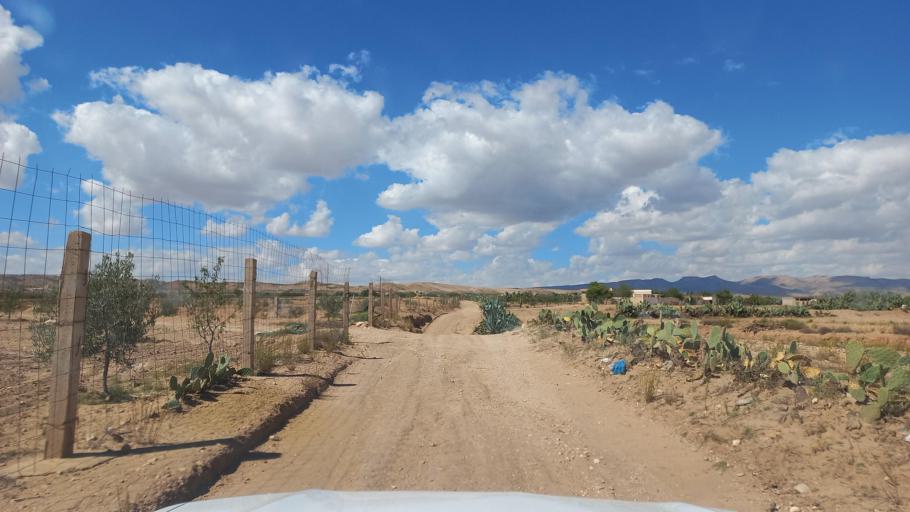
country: TN
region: Al Qasrayn
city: Sbiba
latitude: 35.3528
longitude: 9.0197
